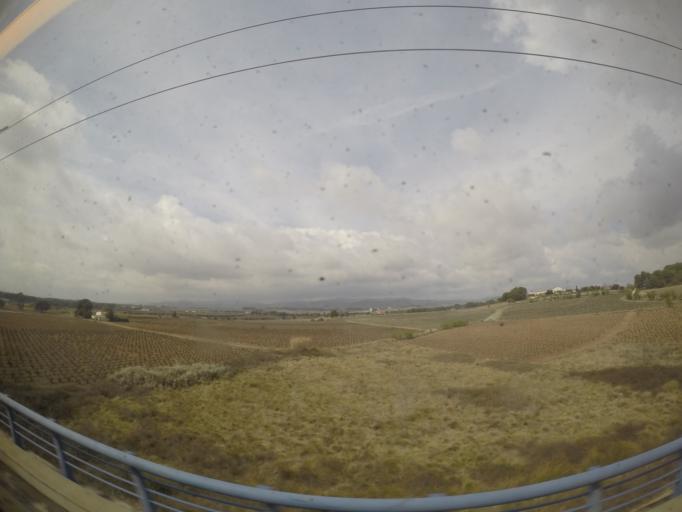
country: ES
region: Catalonia
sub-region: Provincia de Barcelona
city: Castellet
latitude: 41.2687
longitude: 1.5941
